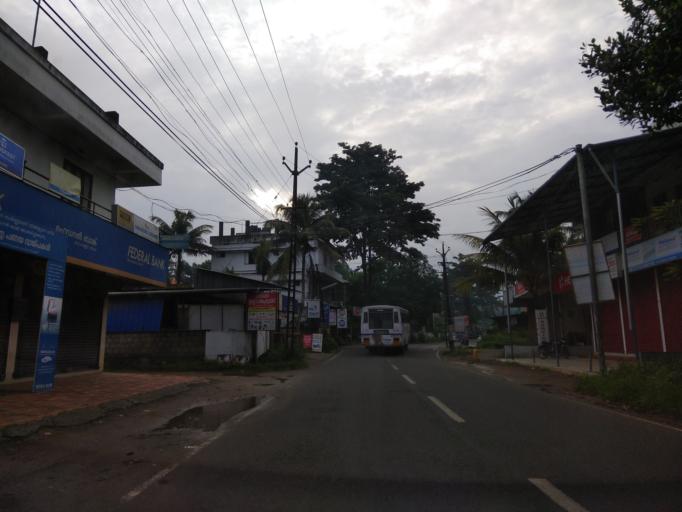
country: IN
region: Kerala
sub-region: Ernakulam
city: Perumbavoor
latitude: 10.1125
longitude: 76.4173
